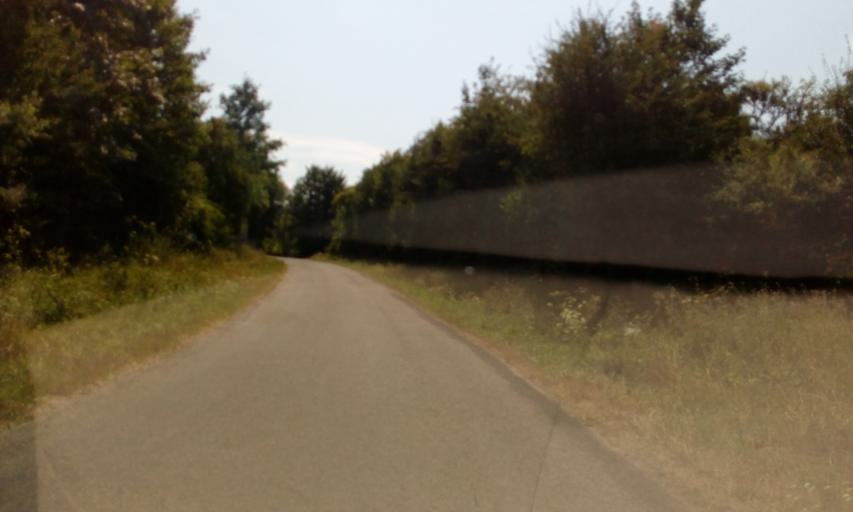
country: FR
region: Lorraine
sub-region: Departement de la Meuse
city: Verdun
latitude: 49.2361
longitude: 5.4705
